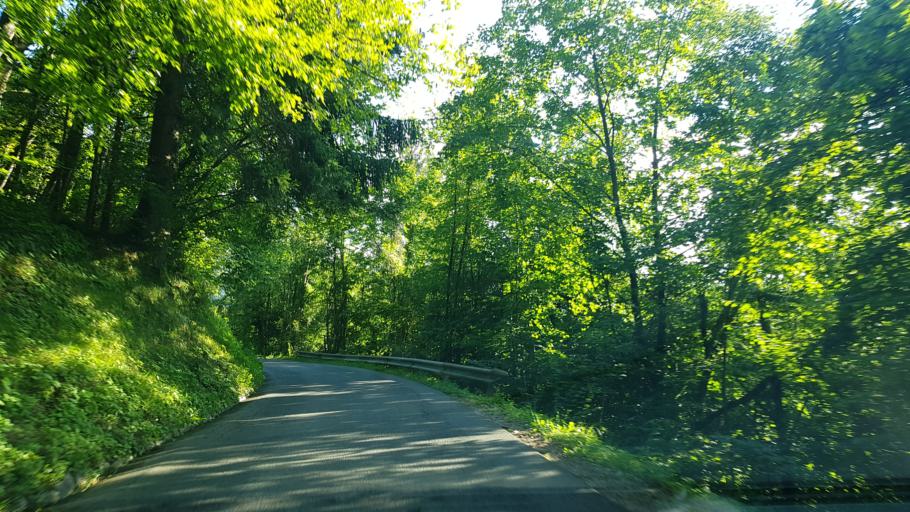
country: SI
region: Cerkno
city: Cerkno
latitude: 46.0846
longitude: 13.9851
